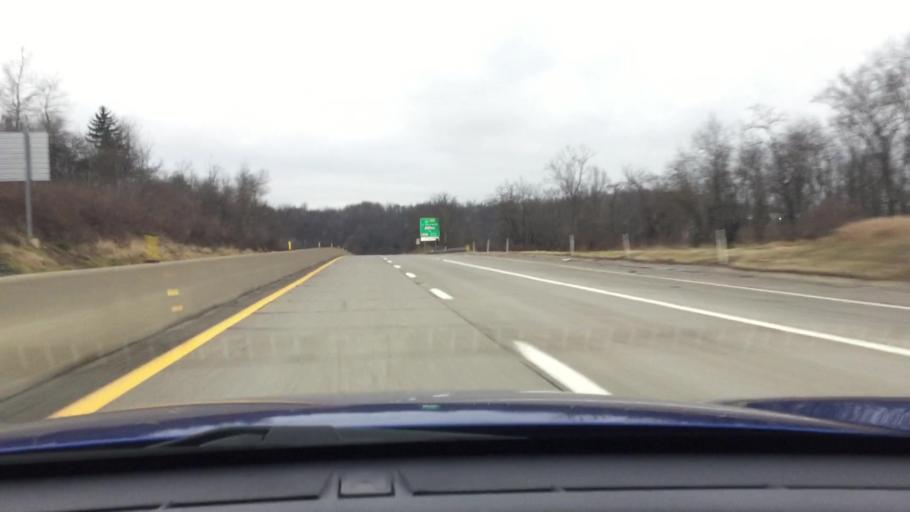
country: US
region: Pennsylvania
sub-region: Allegheny County
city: Imperial
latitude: 40.4258
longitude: -80.2978
